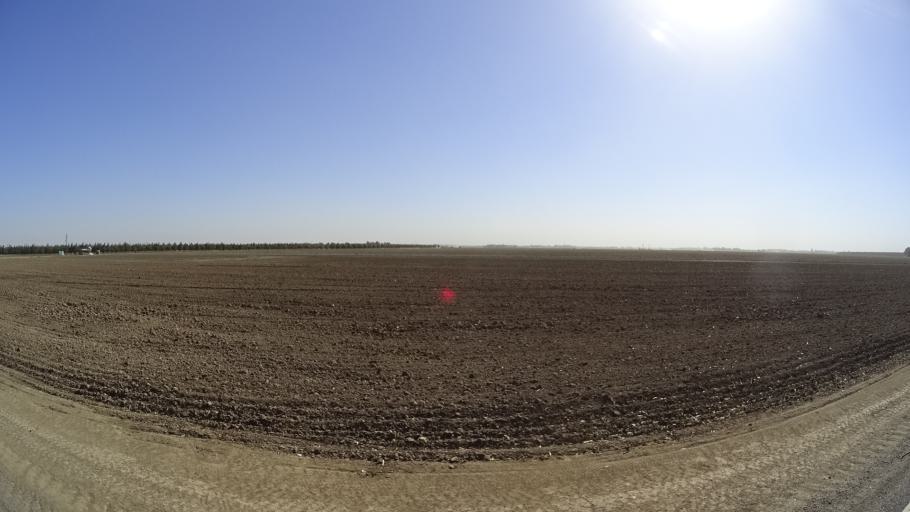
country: US
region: California
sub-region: Yolo County
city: Davis
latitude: 38.5902
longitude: -121.8103
